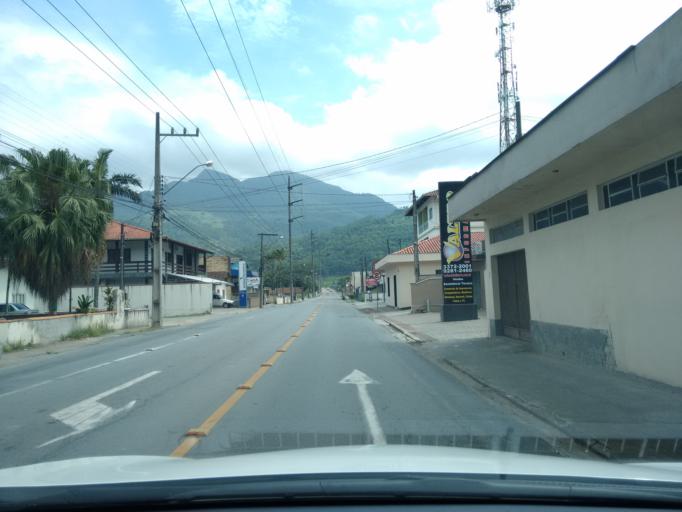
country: BR
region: Santa Catarina
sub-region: Jaragua Do Sul
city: Jaragua do Sul
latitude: -26.4831
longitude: -49.0567
